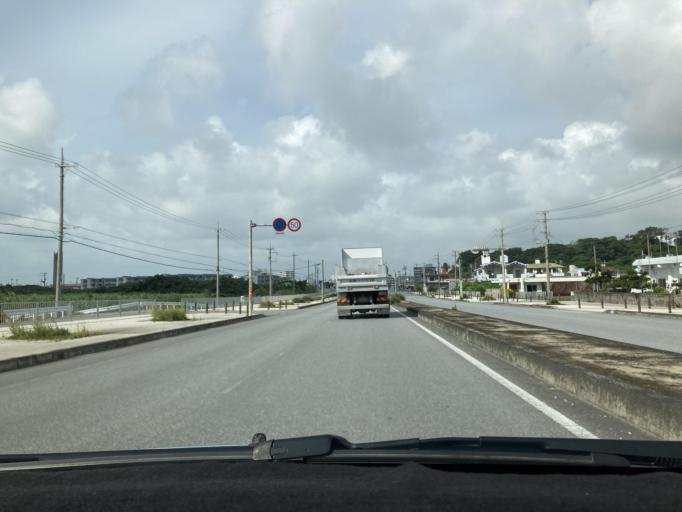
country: JP
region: Okinawa
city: Itoman
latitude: 26.1145
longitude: 127.6684
